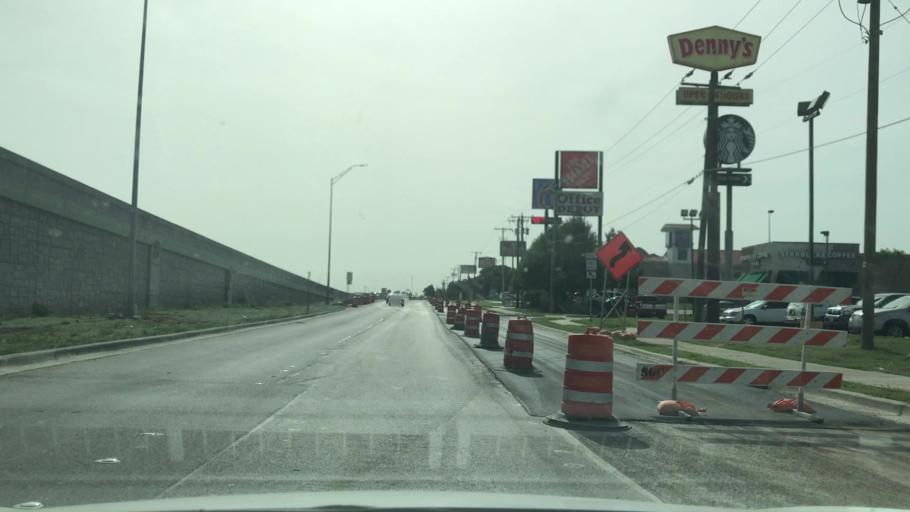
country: US
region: Texas
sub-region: Tarrant County
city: Euless
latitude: 32.8372
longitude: -97.0991
